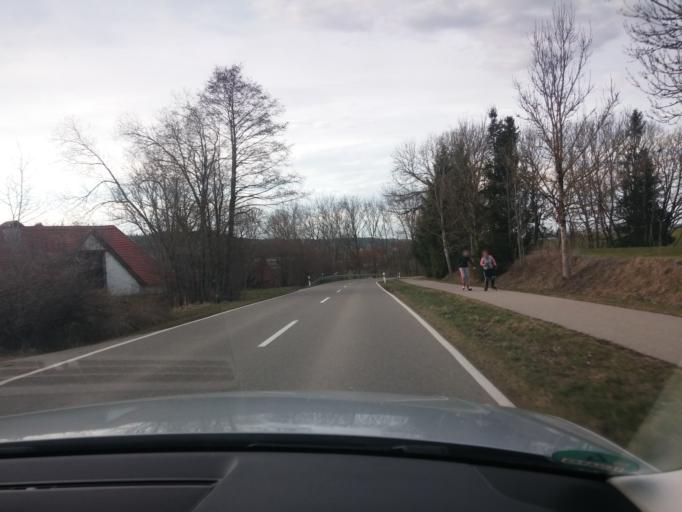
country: DE
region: Bavaria
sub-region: Swabia
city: Woringen
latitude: 47.8852
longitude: 10.2135
